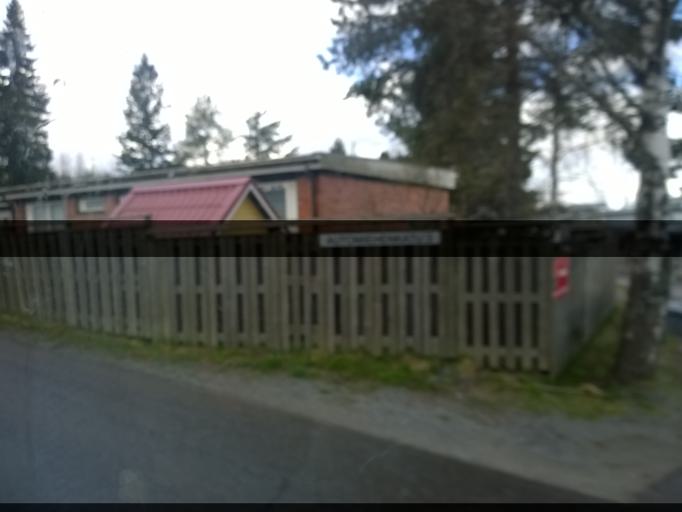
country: FI
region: Pirkanmaa
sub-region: Tampere
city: Tampere
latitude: 61.4551
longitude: 23.7609
